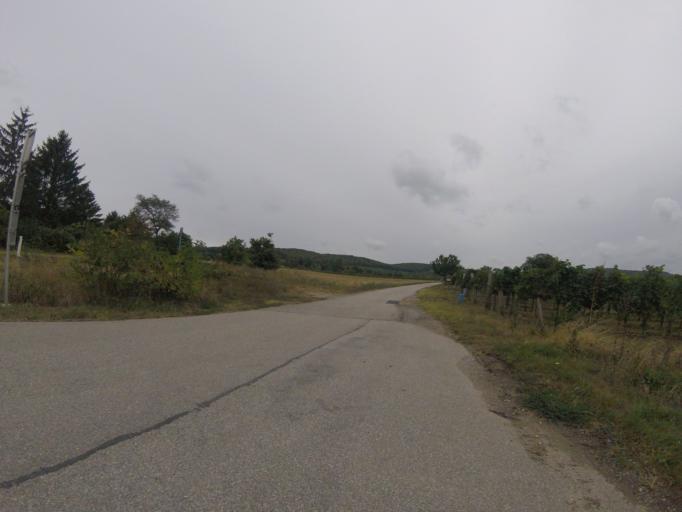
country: AT
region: Burgenland
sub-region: Politischer Bezirk Neusiedl am See
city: Winden am See
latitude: 47.9561
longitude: 16.7388
